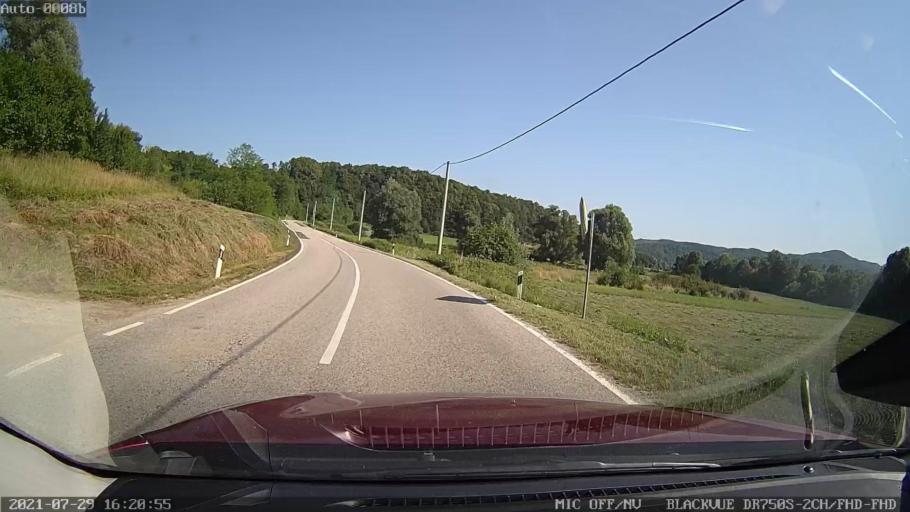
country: HR
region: Varazdinska
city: Lepoglava
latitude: 46.2372
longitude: 15.9642
